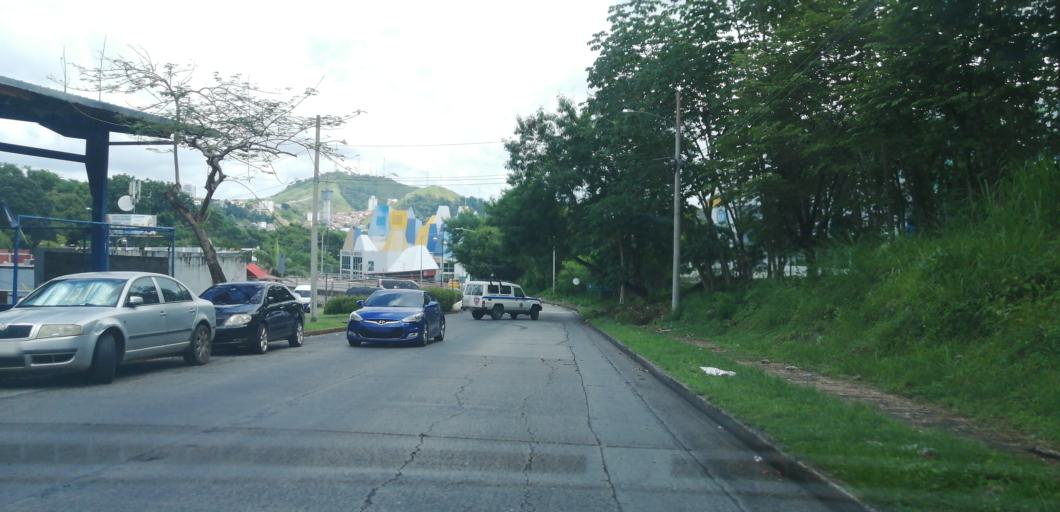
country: PA
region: Panama
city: Panama
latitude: 9.0264
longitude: -79.5192
